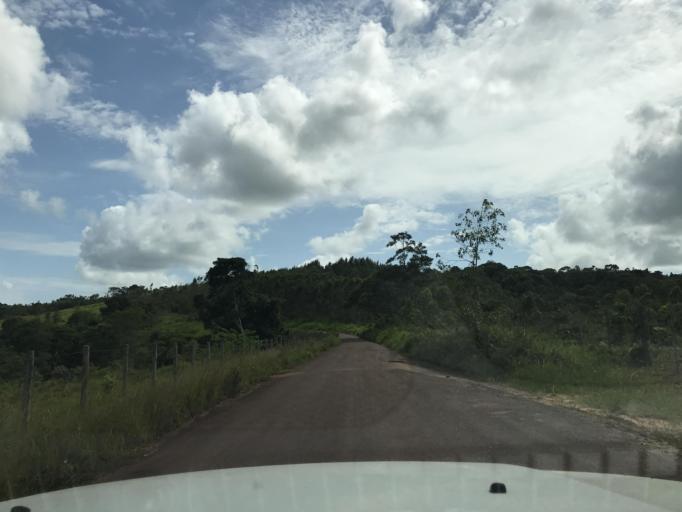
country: BR
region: Bahia
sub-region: Entre Rios
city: Entre Rios
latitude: -12.1743
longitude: -38.1144
